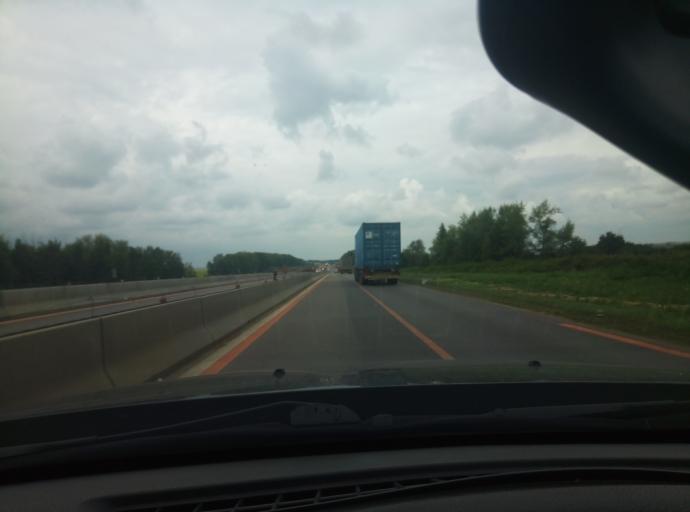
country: RU
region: Tula
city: Dubovka
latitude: 53.9127
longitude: 38.0455
